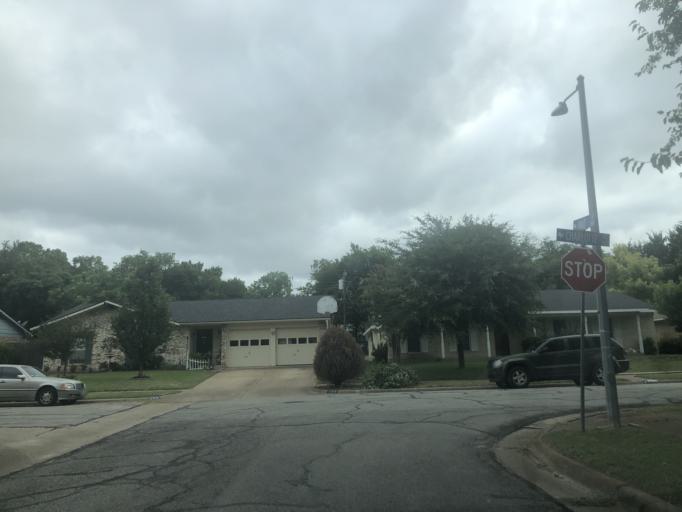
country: US
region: Texas
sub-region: Dallas County
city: Duncanville
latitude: 32.6350
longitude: -96.9053
